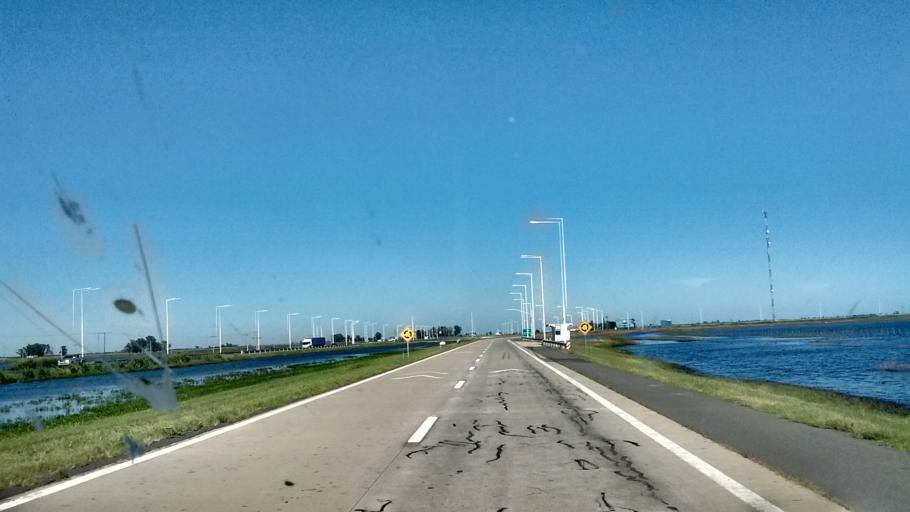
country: AR
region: Cordoba
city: San Francisco
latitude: -31.4631
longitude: -61.8329
